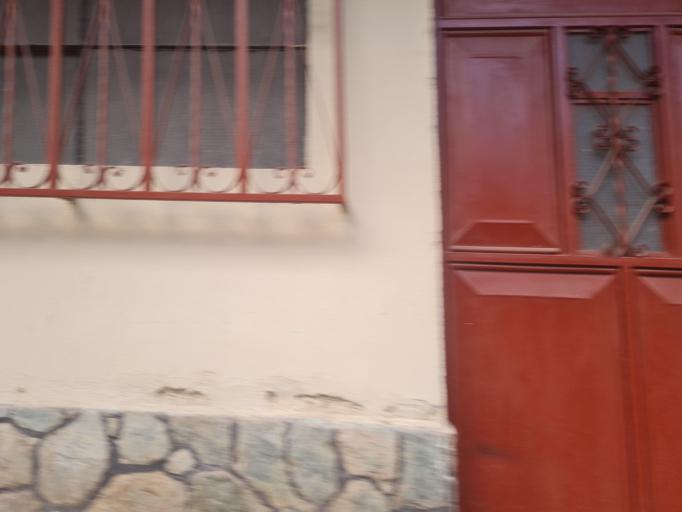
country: GT
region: Quetzaltenango
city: Quetzaltenango
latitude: 14.8313
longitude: -91.5308
